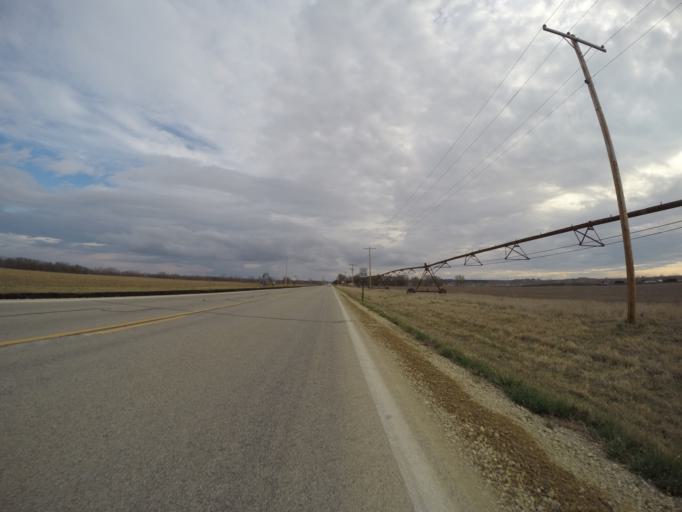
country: US
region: Kansas
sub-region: Riley County
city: Manhattan
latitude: 39.2234
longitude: -96.5578
